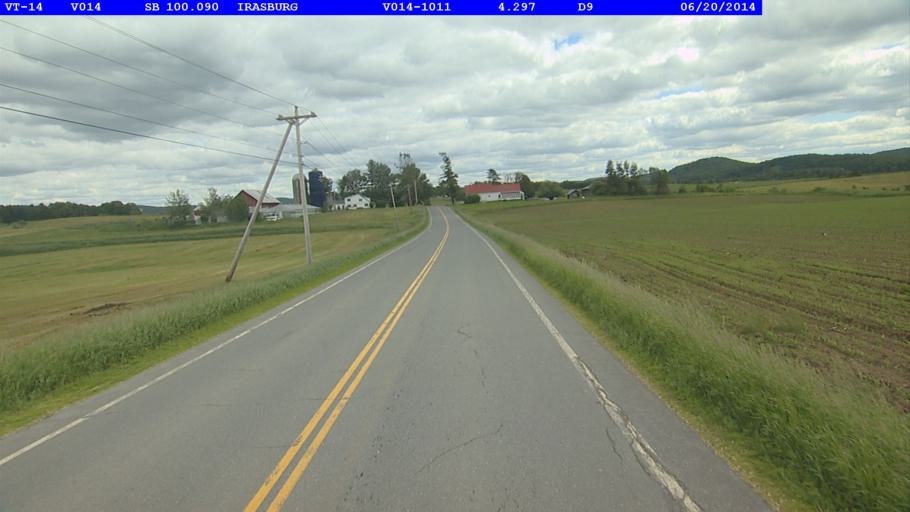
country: US
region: Vermont
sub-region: Orleans County
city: Newport
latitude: 44.8218
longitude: -72.2953
